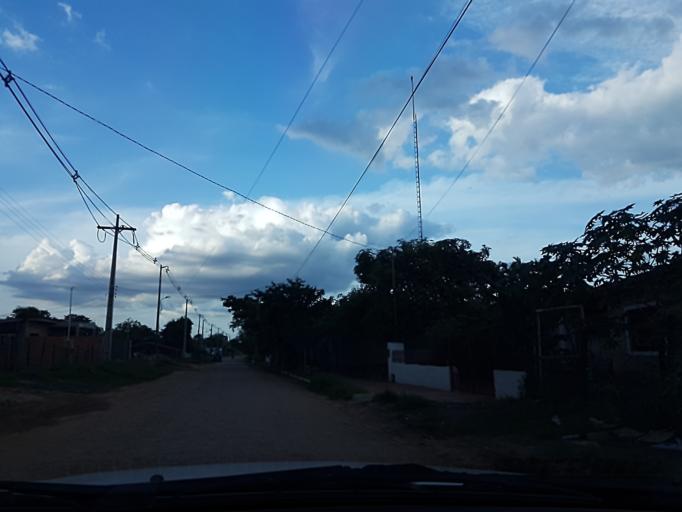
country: PY
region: Central
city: Colonia Mariano Roque Alonso
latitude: -25.2403
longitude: -57.5279
